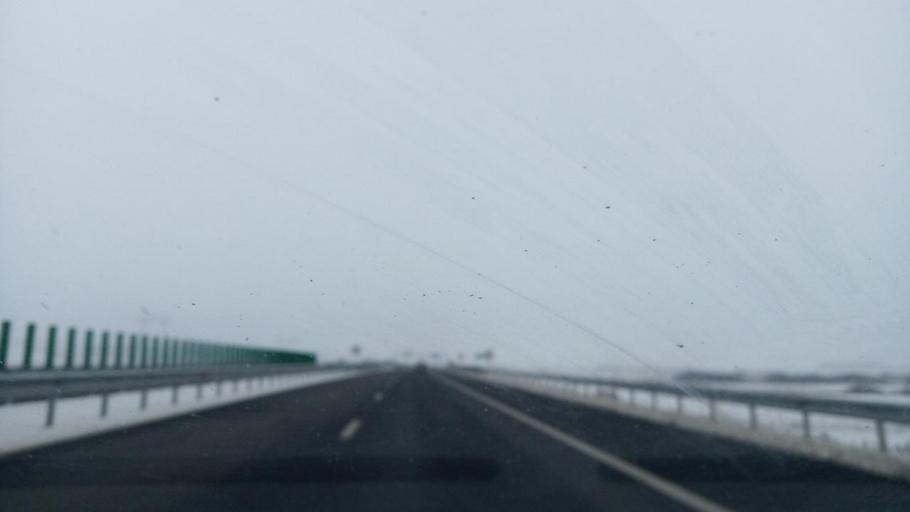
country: RO
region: Bacau
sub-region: Comuna Saucesti
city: Saucesti
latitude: 46.6321
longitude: 26.9377
